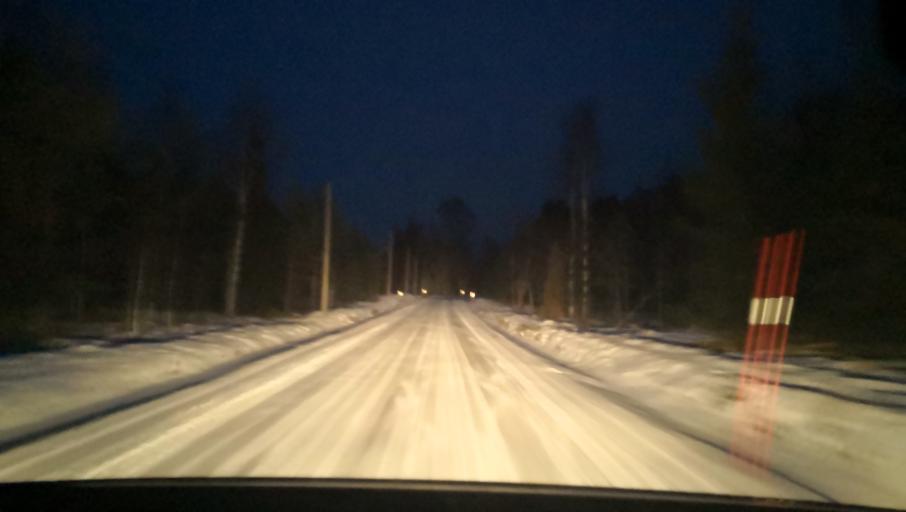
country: SE
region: Uppsala
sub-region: Heby Kommun
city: Tarnsjo
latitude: 60.2669
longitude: 16.7926
